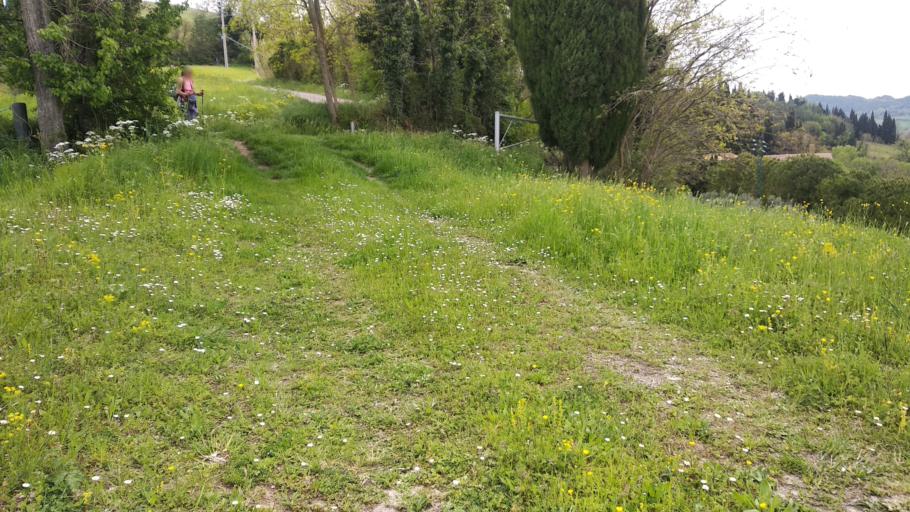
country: IT
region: Emilia-Romagna
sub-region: Provincia di Ravenna
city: Fognano
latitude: 44.1993
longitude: 11.7615
